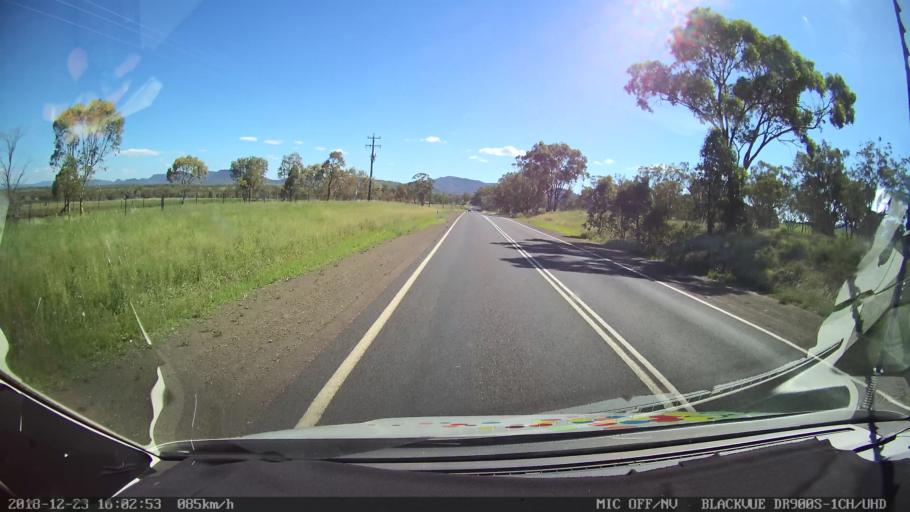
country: AU
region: New South Wales
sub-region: Tamworth Municipality
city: Phillip
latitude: -31.2371
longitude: 150.8054
